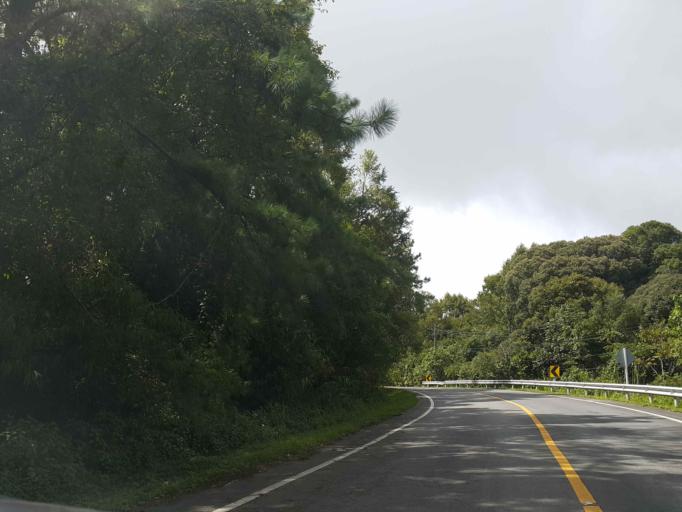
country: TH
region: Chiang Mai
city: Mae Chaem
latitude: 18.5353
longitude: 98.4932
